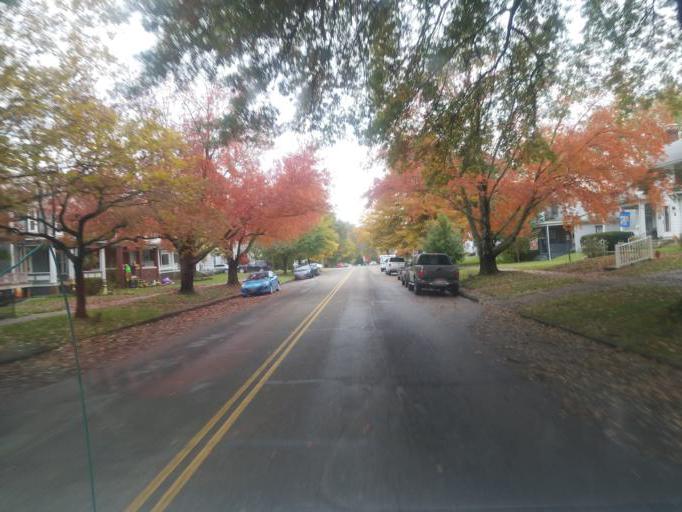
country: US
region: Ohio
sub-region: Washington County
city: Marietta
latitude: 39.4244
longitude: -81.4639
